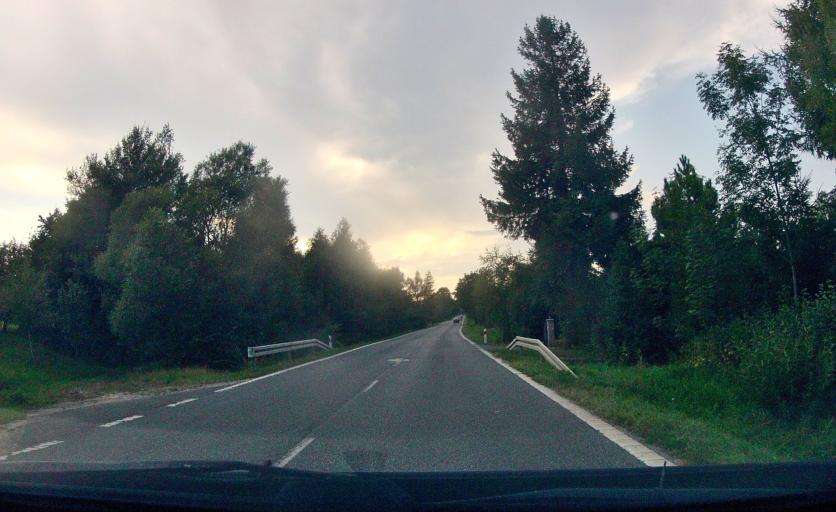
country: PL
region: Subcarpathian Voivodeship
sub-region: Powiat krosnienski
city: Dukla
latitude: 49.5633
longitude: 21.5994
